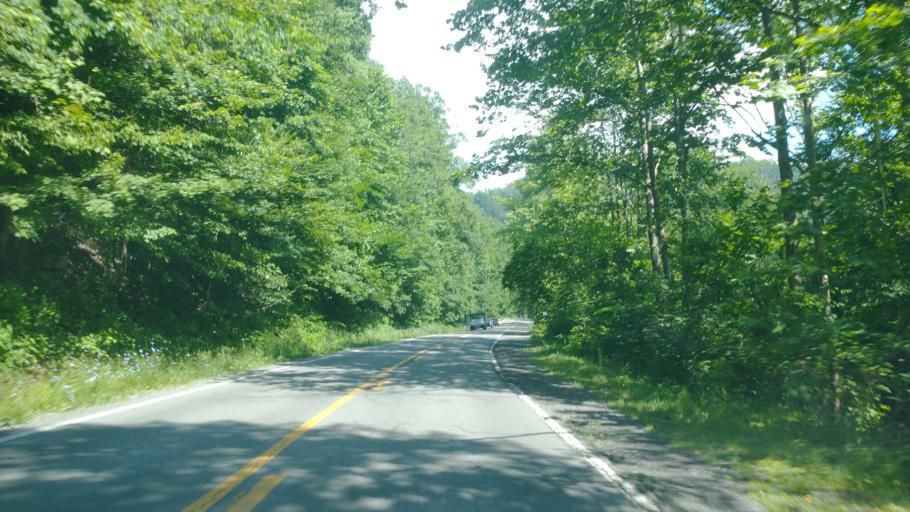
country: US
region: West Virginia
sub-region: McDowell County
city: Welch
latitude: 37.4251
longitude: -81.5503
